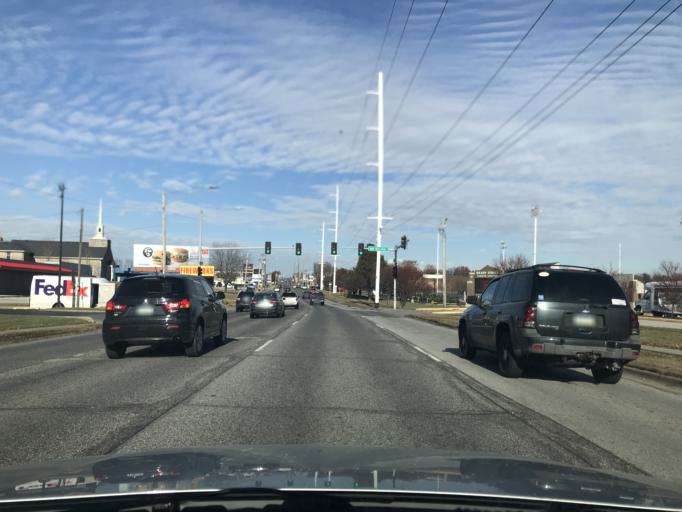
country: US
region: Iowa
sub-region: Scott County
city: Davenport
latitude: 41.5543
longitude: -90.5691
